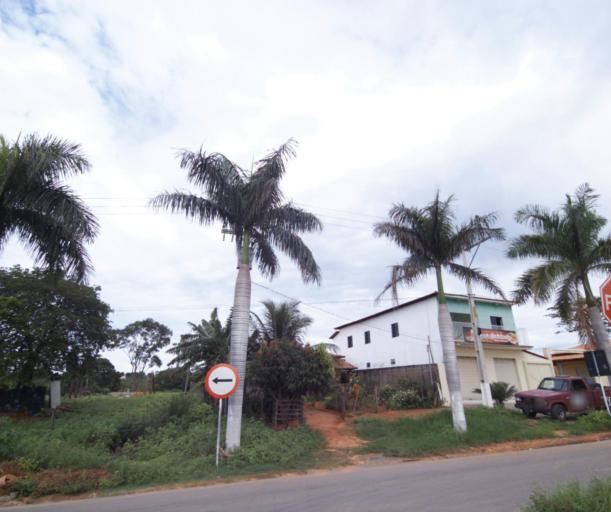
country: BR
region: Bahia
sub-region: Carinhanha
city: Carinhanha
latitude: -14.1755
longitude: -44.5304
